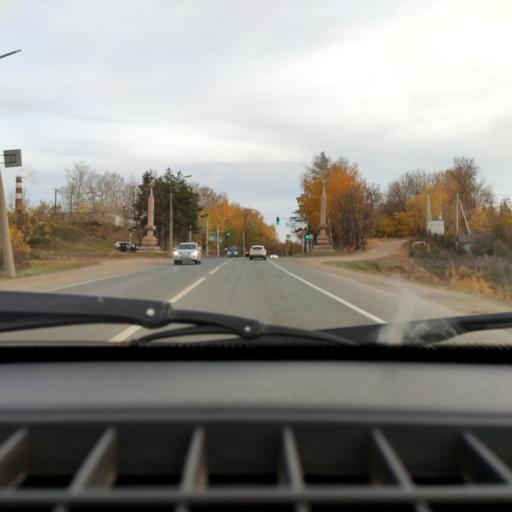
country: RU
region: Bashkortostan
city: Avdon
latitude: 54.6805
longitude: 55.8070
